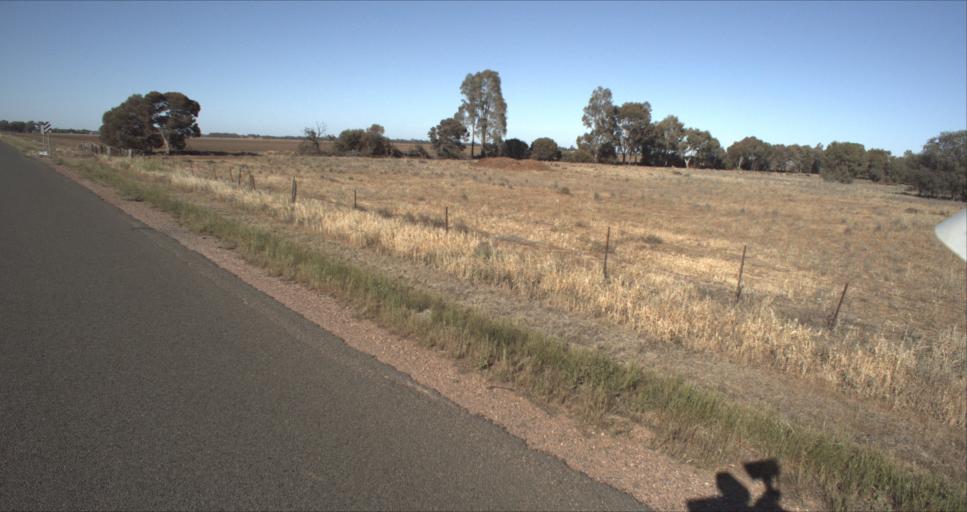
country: AU
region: New South Wales
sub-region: Leeton
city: Leeton
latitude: -34.5662
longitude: 146.2644
